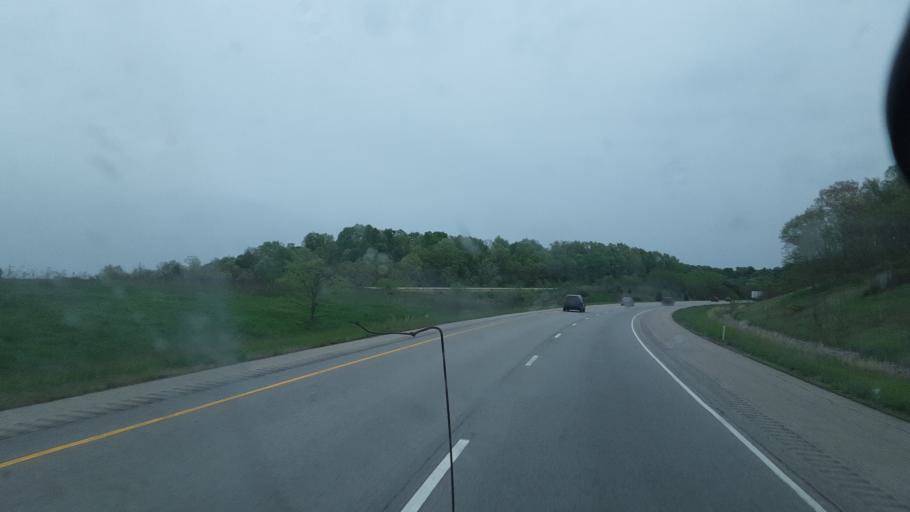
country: US
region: Indiana
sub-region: Crawford County
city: English
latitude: 38.2315
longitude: -86.6280
